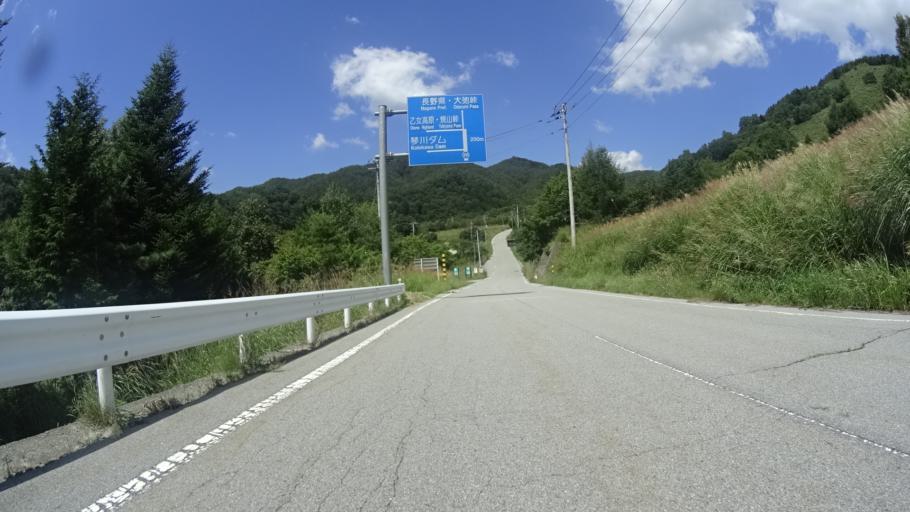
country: JP
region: Yamanashi
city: Enzan
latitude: 35.8074
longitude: 138.6576
